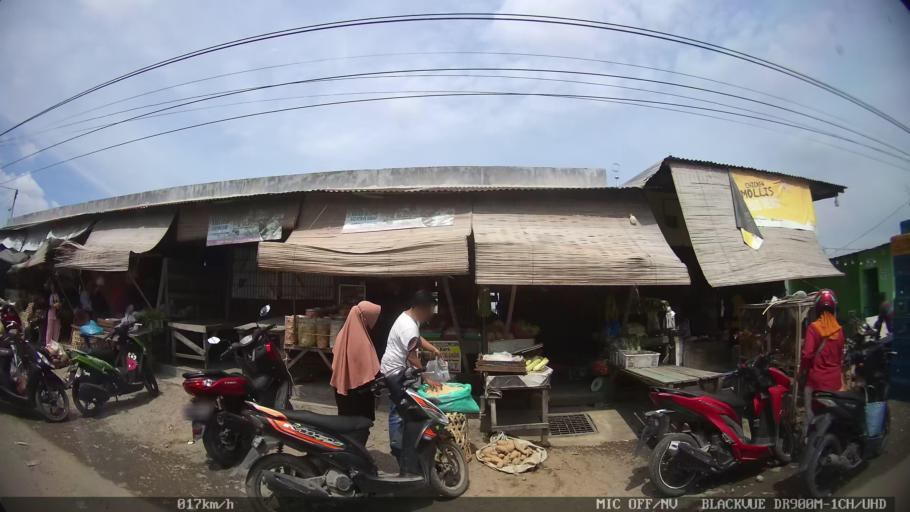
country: ID
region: North Sumatra
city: Medan
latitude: 3.6495
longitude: 98.6878
